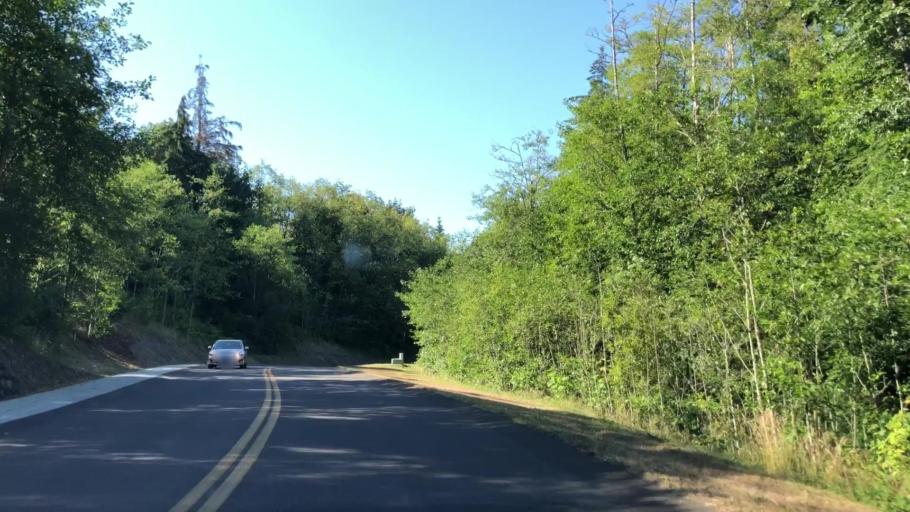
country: US
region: Washington
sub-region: Kitsap County
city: Indianola
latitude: 47.7703
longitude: -122.5256
